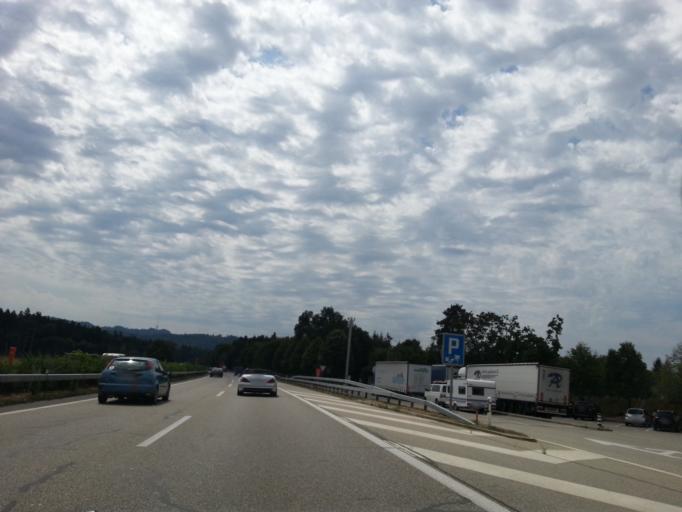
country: CH
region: Bern
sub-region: Emmental District
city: Hindelbank
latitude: 47.0435
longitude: 7.5292
